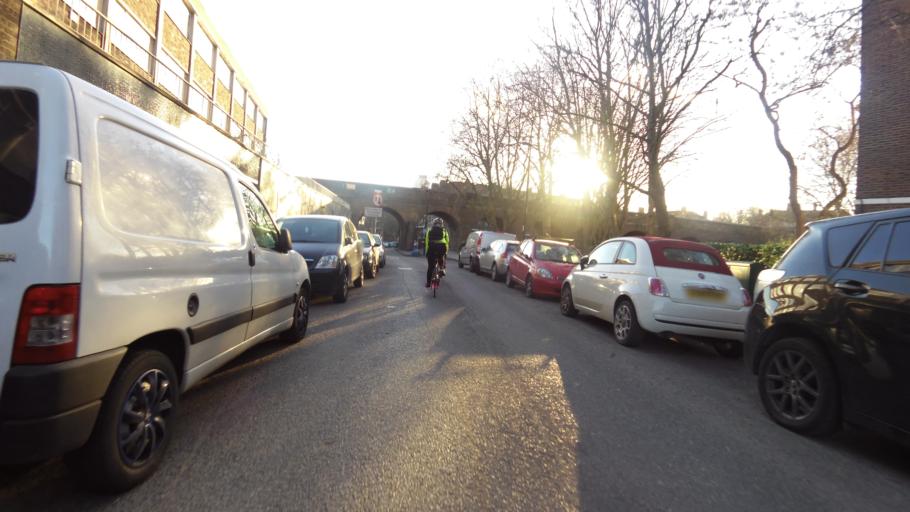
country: GB
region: England
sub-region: Greater London
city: Blackheath
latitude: 51.4788
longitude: -0.0208
